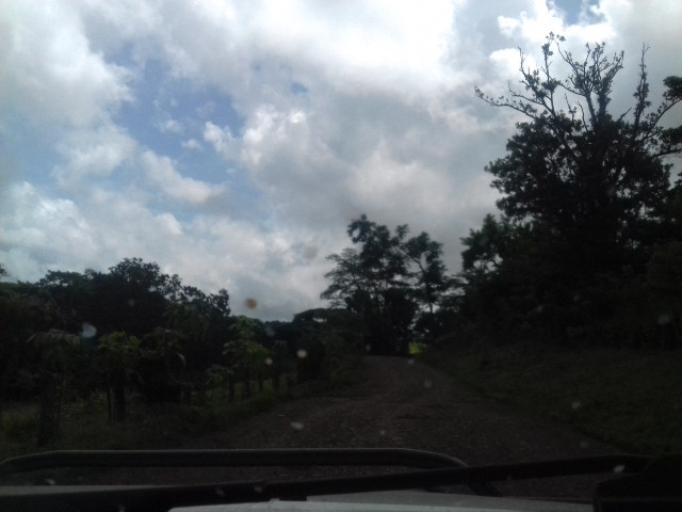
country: NI
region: Matagalpa
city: Matiguas
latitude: 12.9000
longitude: -85.3640
